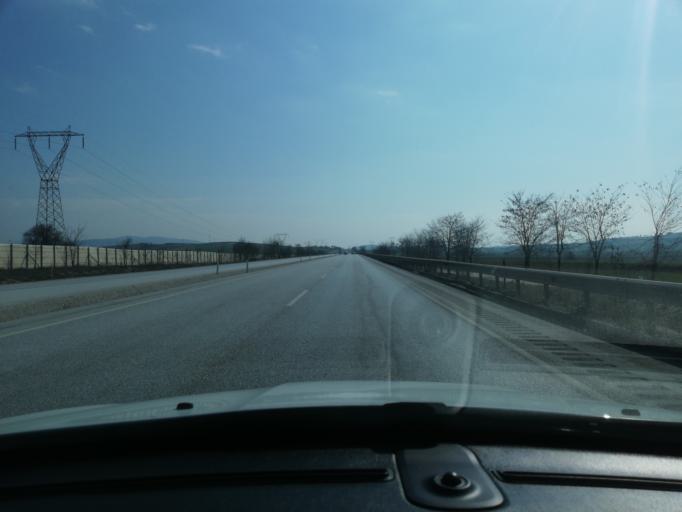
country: TR
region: Cankiri
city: Kursunlu
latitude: 40.8423
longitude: 33.1721
